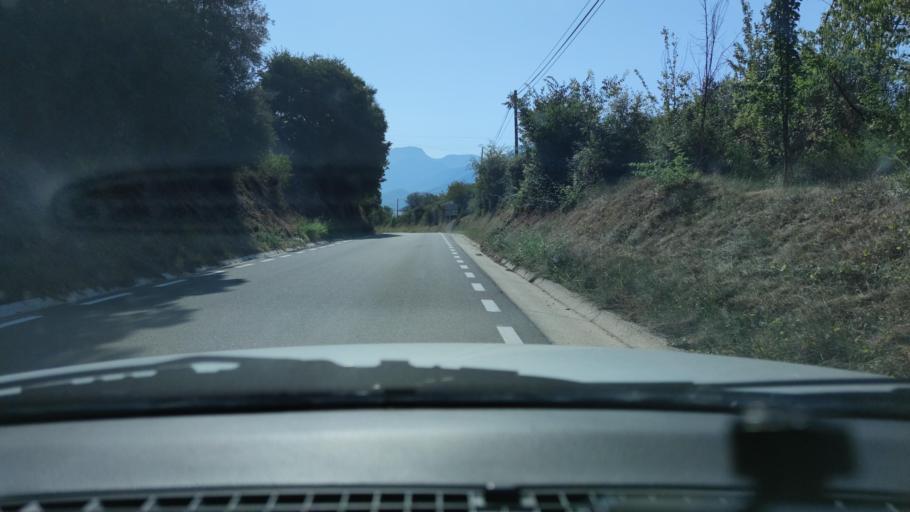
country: ES
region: Catalonia
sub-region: Provincia de Lleida
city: Tremp
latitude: 42.2110
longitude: 0.9424
